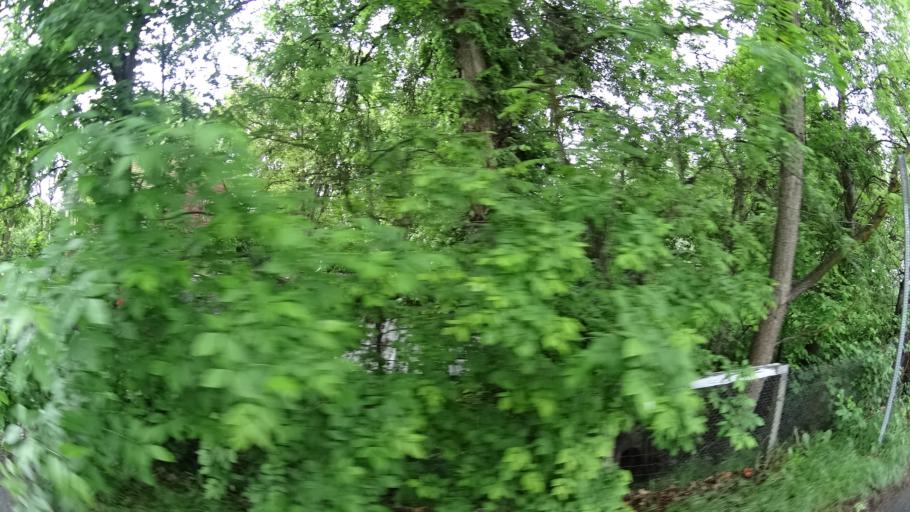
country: US
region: Idaho
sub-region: Ada County
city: Eagle
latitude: 43.6942
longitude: -116.3549
